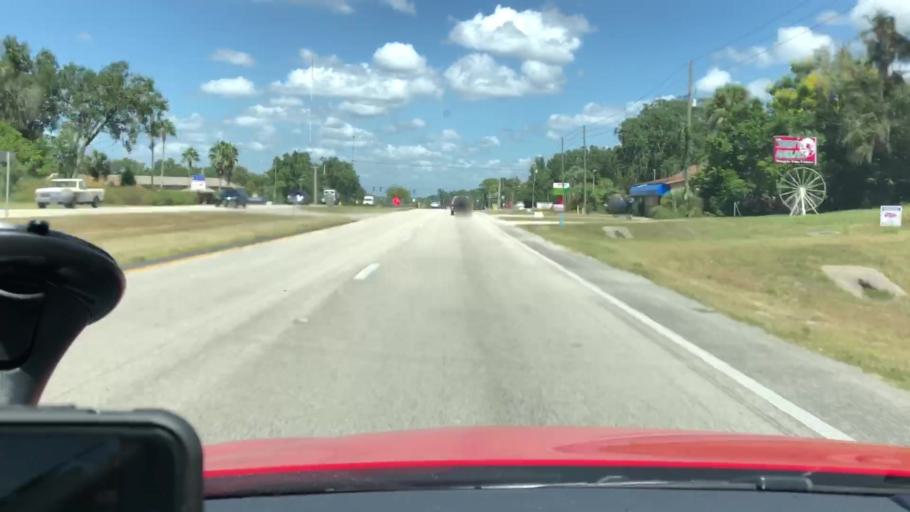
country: US
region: Florida
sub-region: Volusia County
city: Orange City
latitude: 28.9675
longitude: -81.2986
